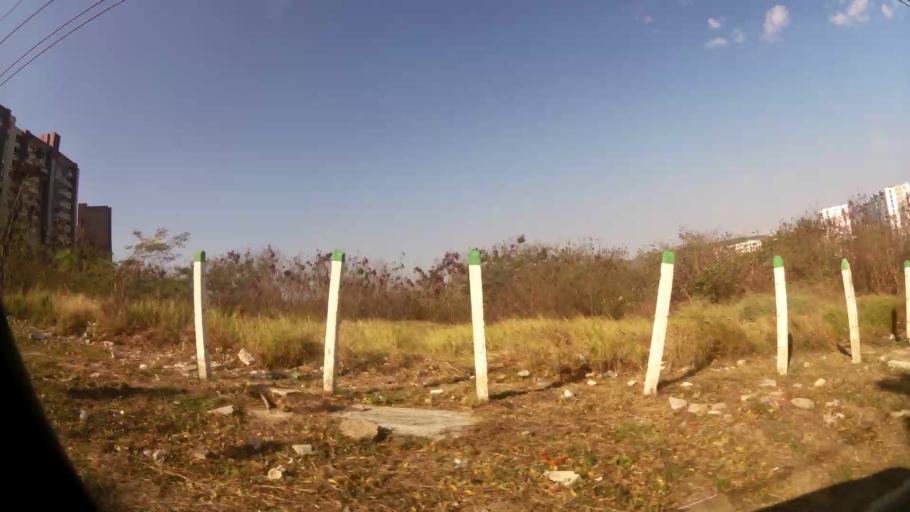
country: CO
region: Atlantico
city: Barranquilla
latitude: 11.0053
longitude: -74.8353
